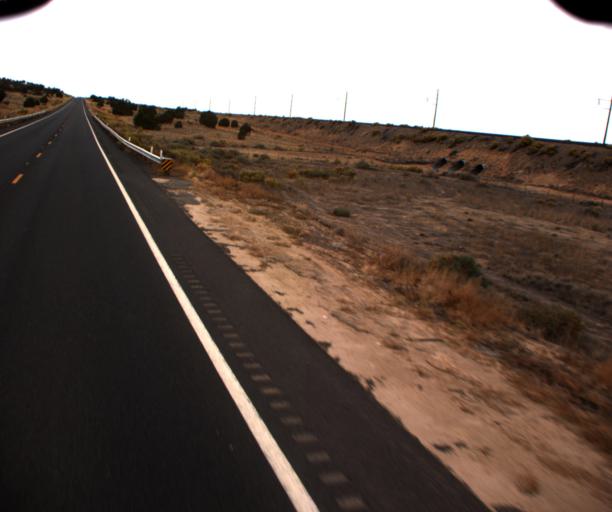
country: US
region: Arizona
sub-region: Coconino County
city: Kaibito
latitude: 36.4549
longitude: -110.7070
